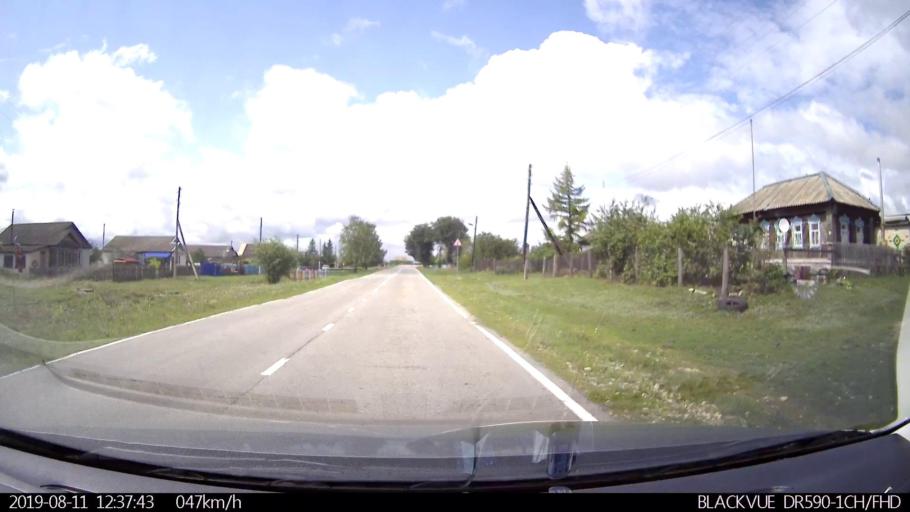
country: RU
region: Ulyanovsk
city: Ignatovka
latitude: 53.8242
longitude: 47.8120
